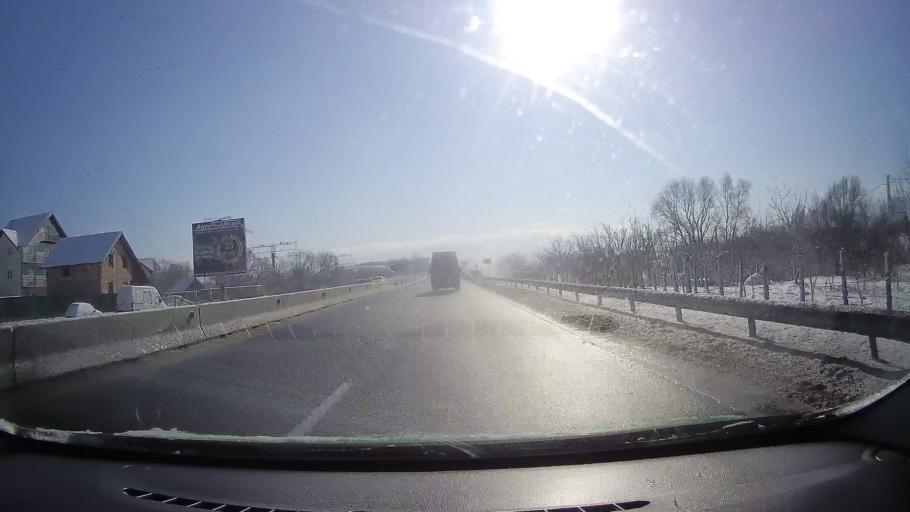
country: RO
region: Sibiu
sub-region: Comuna Selimbar
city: Selimbar
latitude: 45.7677
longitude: 24.1842
